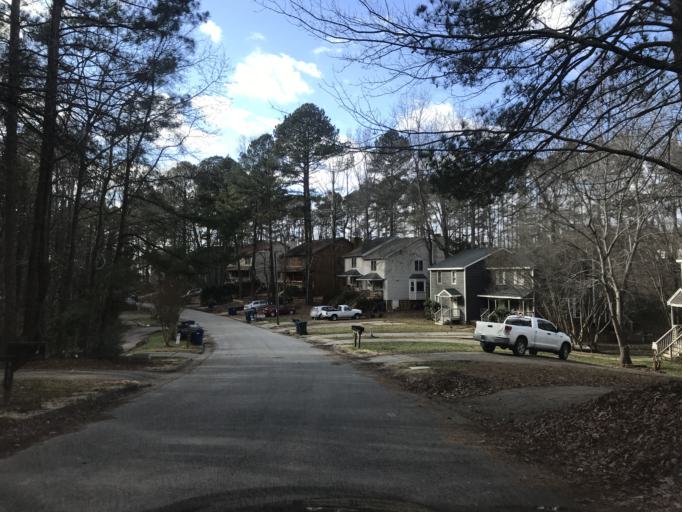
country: US
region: North Carolina
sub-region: Wake County
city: West Raleigh
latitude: 35.7714
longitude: -78.7182
